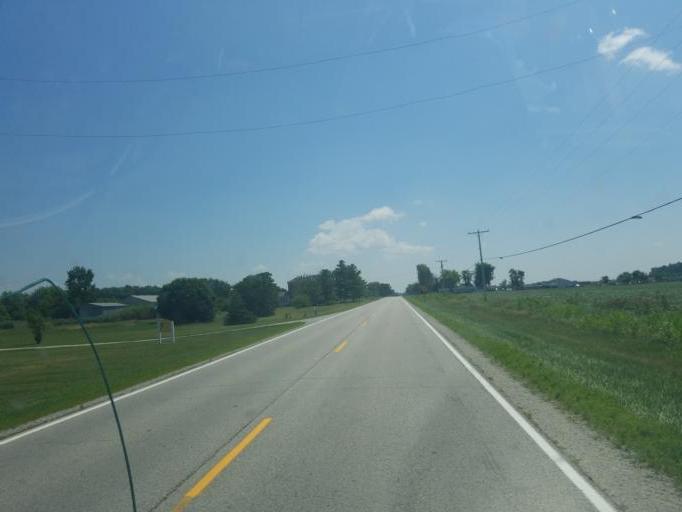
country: US
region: Ohio
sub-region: Shelby County
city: Anna
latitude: 40.4268
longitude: -84.1771
